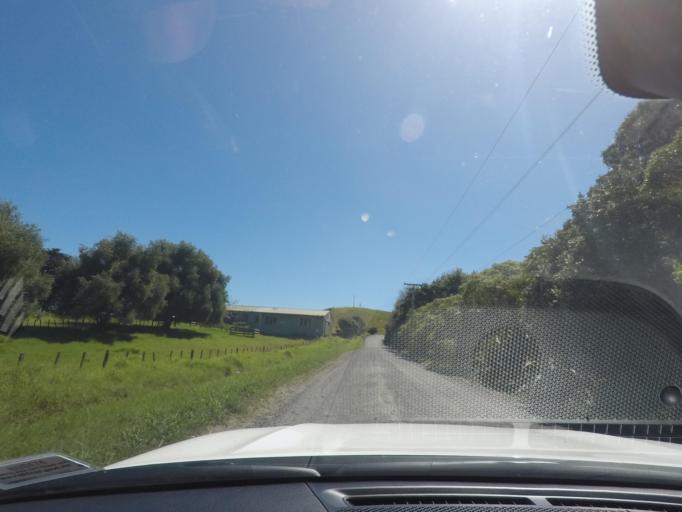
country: NZ
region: Auckland
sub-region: Auckland
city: Parakai
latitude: -36.5816
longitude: 174.3136
